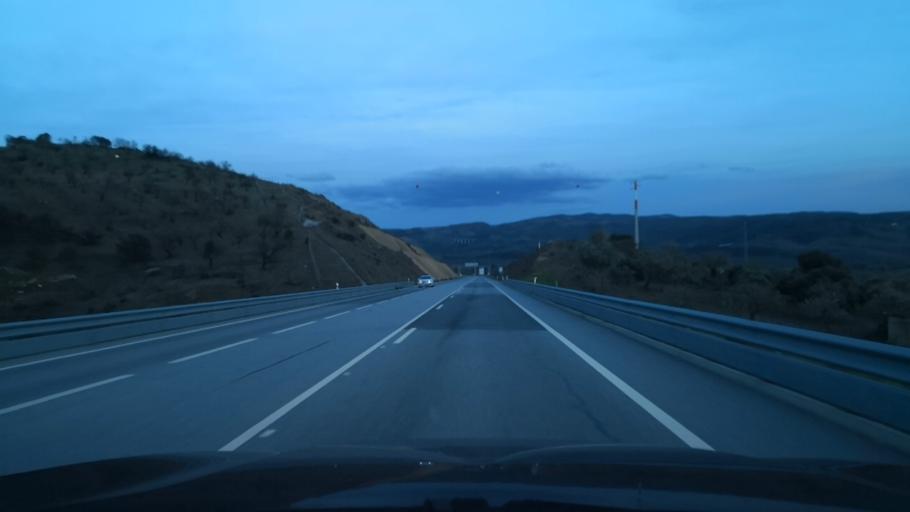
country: PT
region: Braganca
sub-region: Braganca Municipality
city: Vila Flor
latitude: 41.3226
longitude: -7.0961
